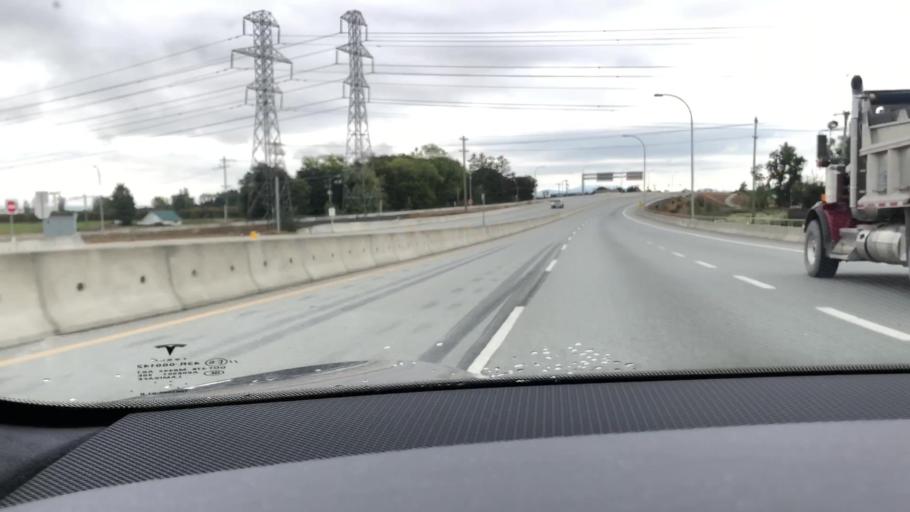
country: CA
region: British Columbia
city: Ladner
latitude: 49.0932
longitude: -123.0258
